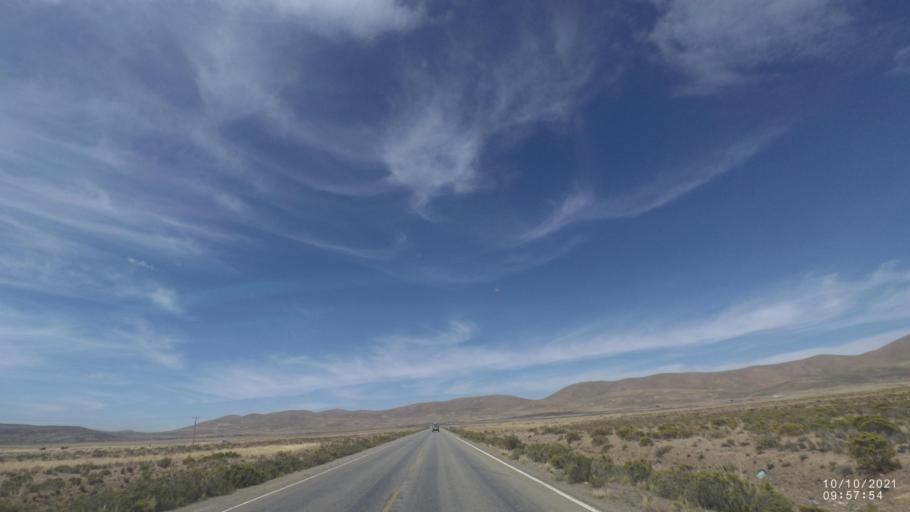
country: BO
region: La Paz
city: Colquiri
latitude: -17.3433
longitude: -67.3899
